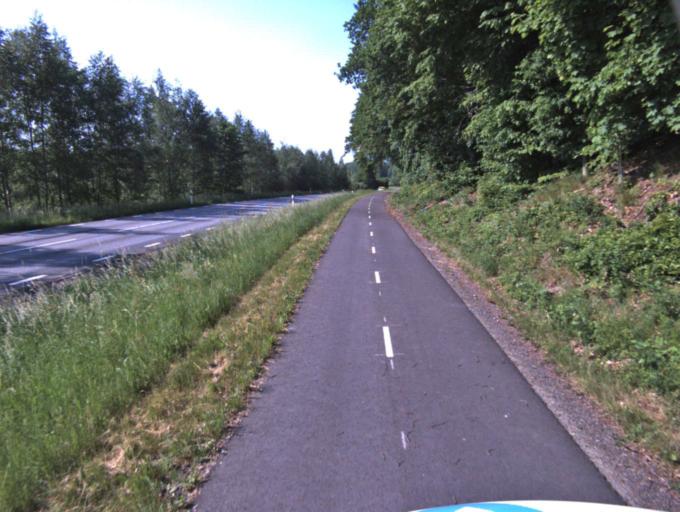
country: SE
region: Skane
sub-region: Kristianstads Kommun
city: Tollarp
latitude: 56.1549
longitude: 14.2668
